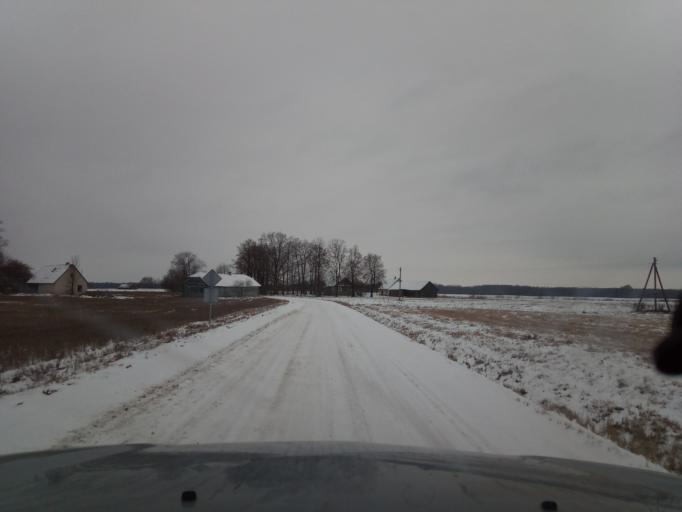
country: LT
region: Vilnius County
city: Ukmerge
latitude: 55.4859
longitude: 24.5914
